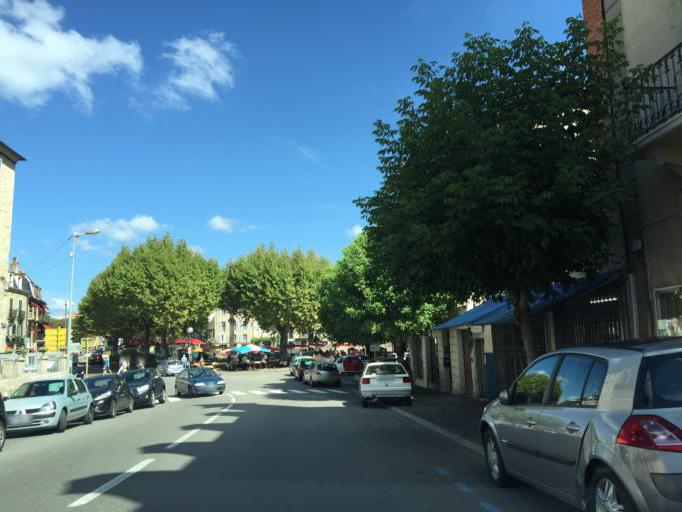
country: FR
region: Midi-Pyrenees
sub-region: Departement de l'Aveyron
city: Villefranche-de-Rouergue
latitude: 44.3483
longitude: 2.0374
